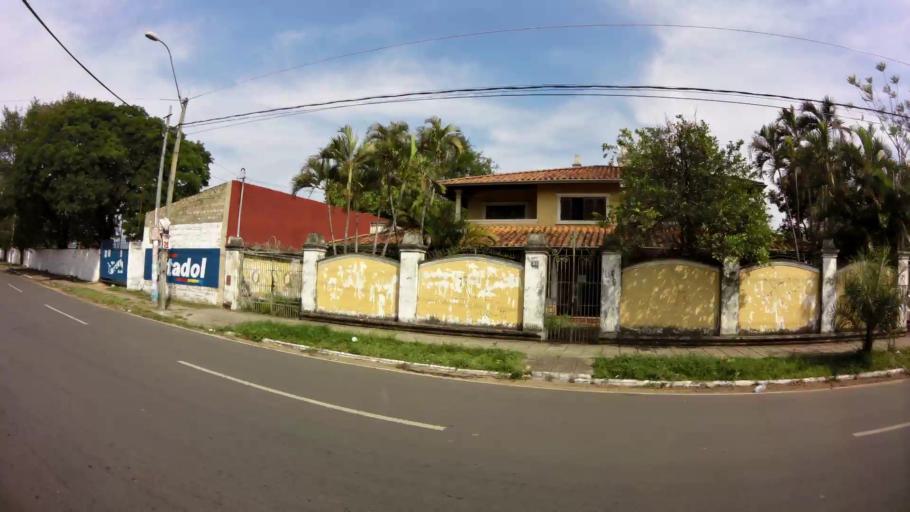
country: PY
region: Central
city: Fernando de la Mora
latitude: -25.2755
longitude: -57.5508
